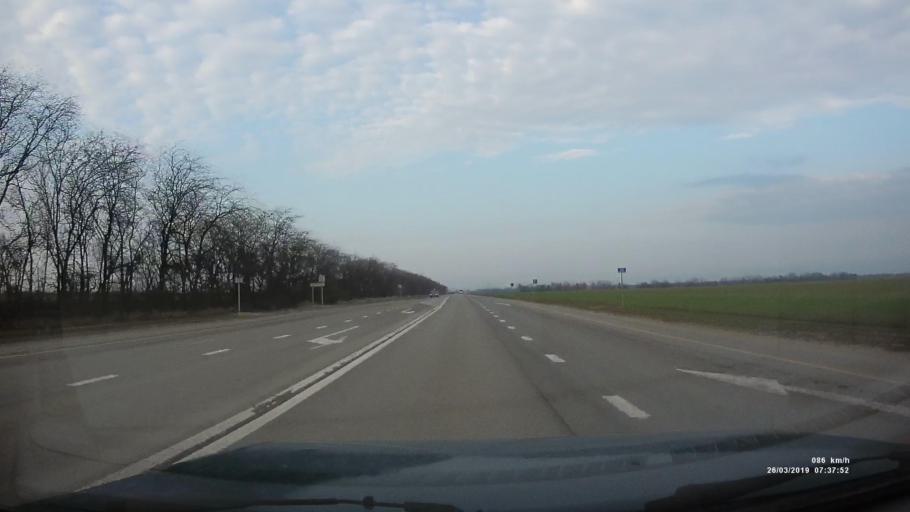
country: RU
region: Rostov
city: Novobessergenovka
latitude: 47.2012
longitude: 38.6935
